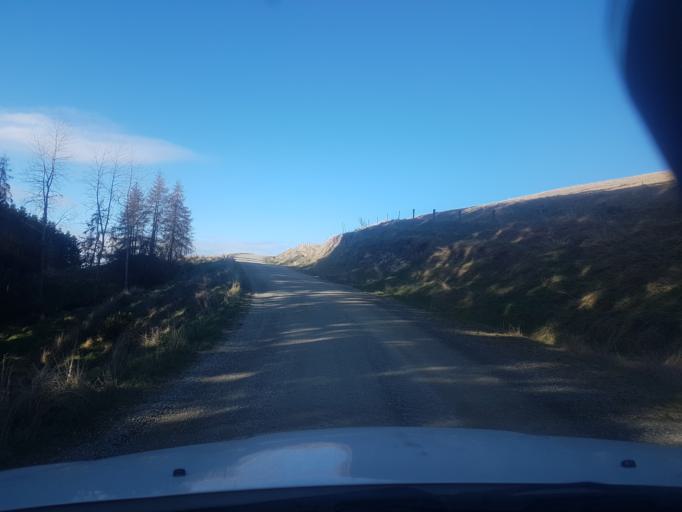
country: NZ
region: Canterbury
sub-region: Timaru District
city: Pleasant Point
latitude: -44.1670
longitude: 170.9130
